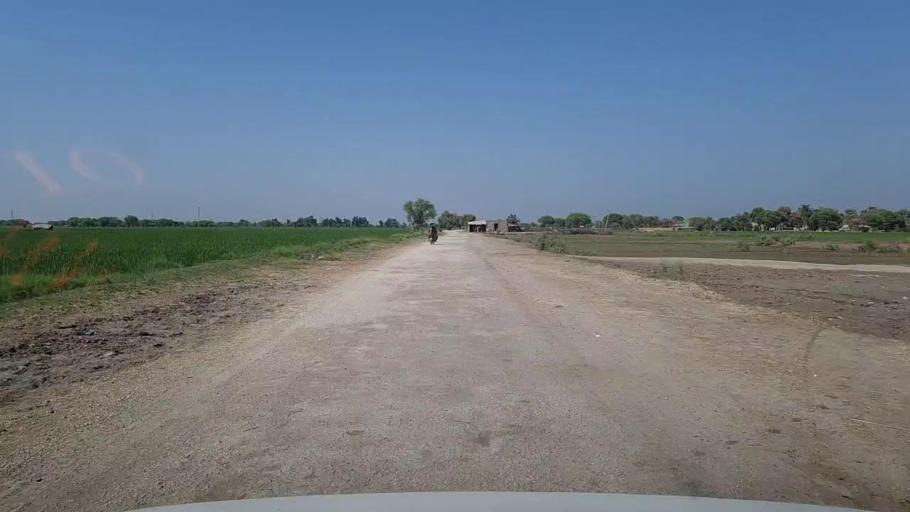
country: PK
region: Sindh
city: Kandhkot
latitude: 28.3235
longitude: 69.3665
